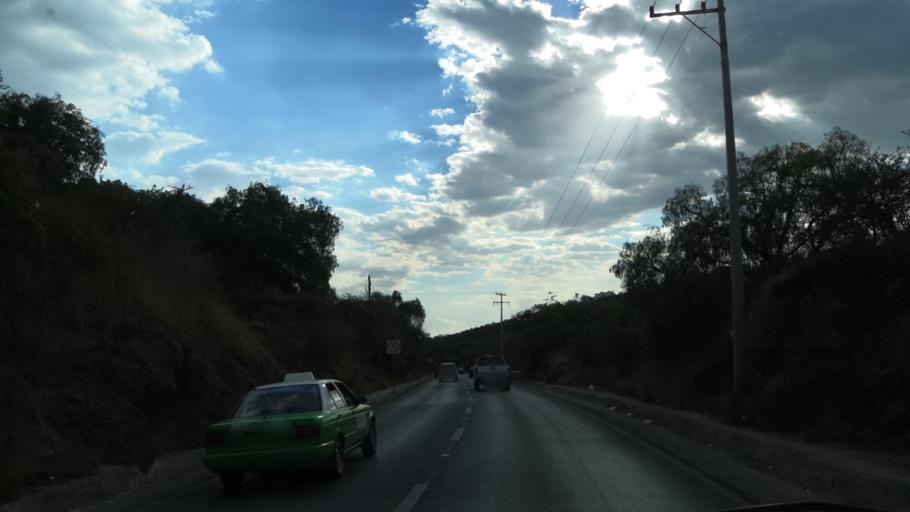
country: MX
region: Guanajuato
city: Guanajuato
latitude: 21.0092
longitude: -101.2716
